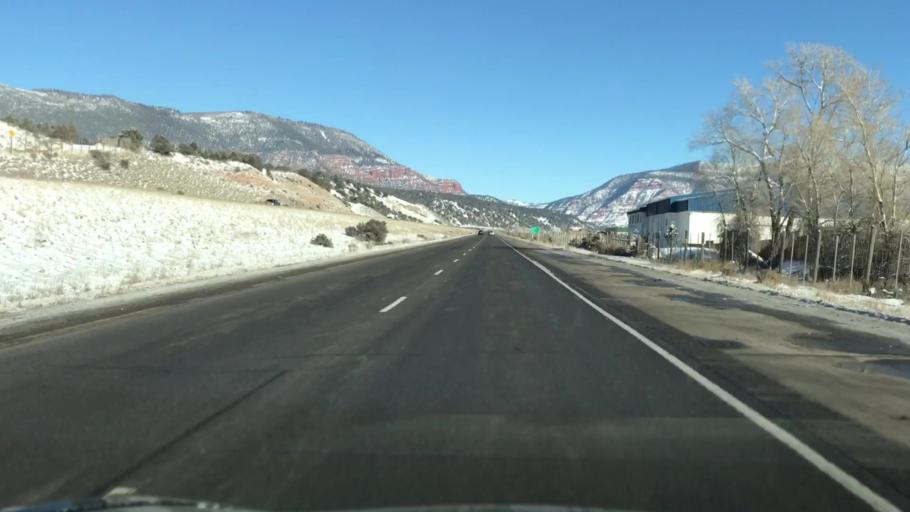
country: US
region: Colorado
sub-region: Eagle County
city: Eagle
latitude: 39.6657
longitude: -106.8158
